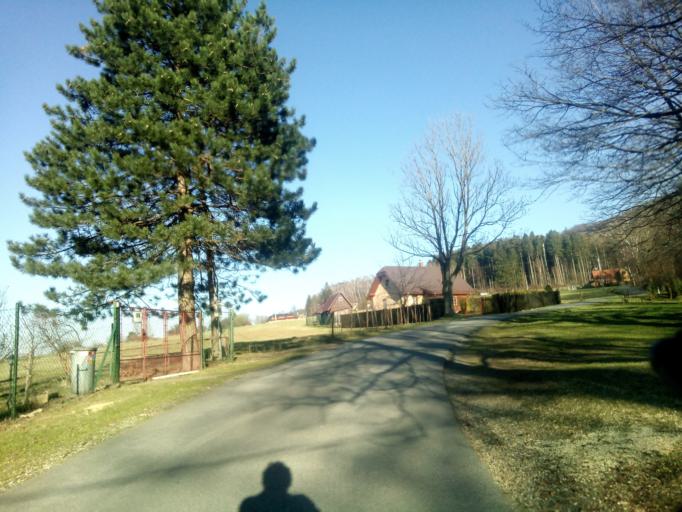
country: CZ
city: Dobratice
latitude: 49.6447
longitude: 18.4768
